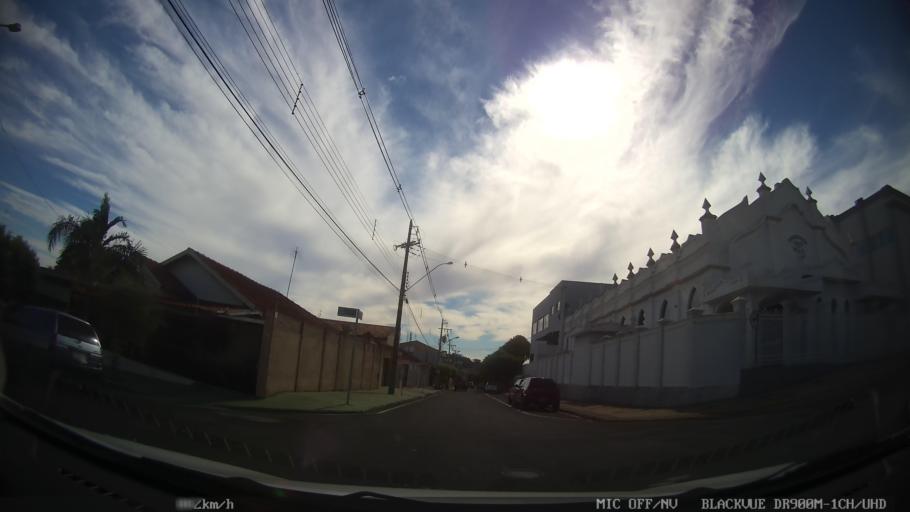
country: BR
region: Sao Paulo
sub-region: Catanduva
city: Catanduva
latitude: -21.1339
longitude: -48.9660
